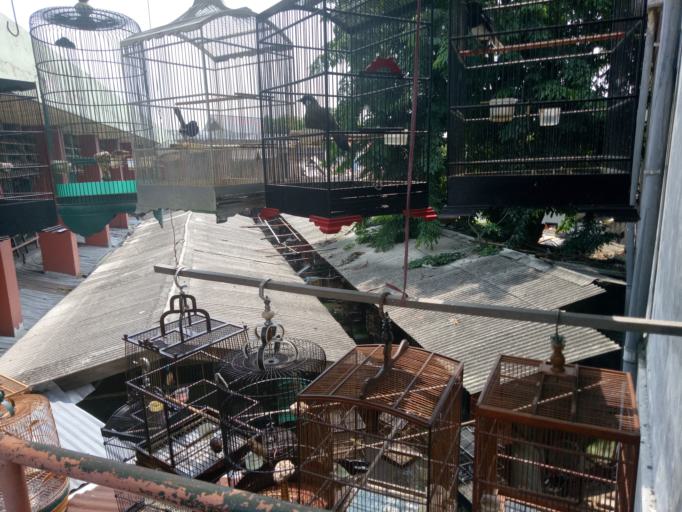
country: ID
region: East Java
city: Jagirsidosermo
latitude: -7.2978
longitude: 112.7605
